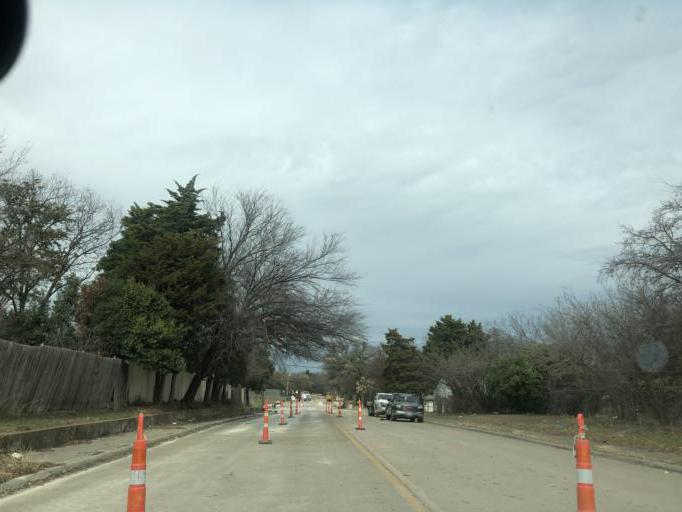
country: US
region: Texas
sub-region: Dallas County
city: Duncanville
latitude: 32.6728
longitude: -96.8292
